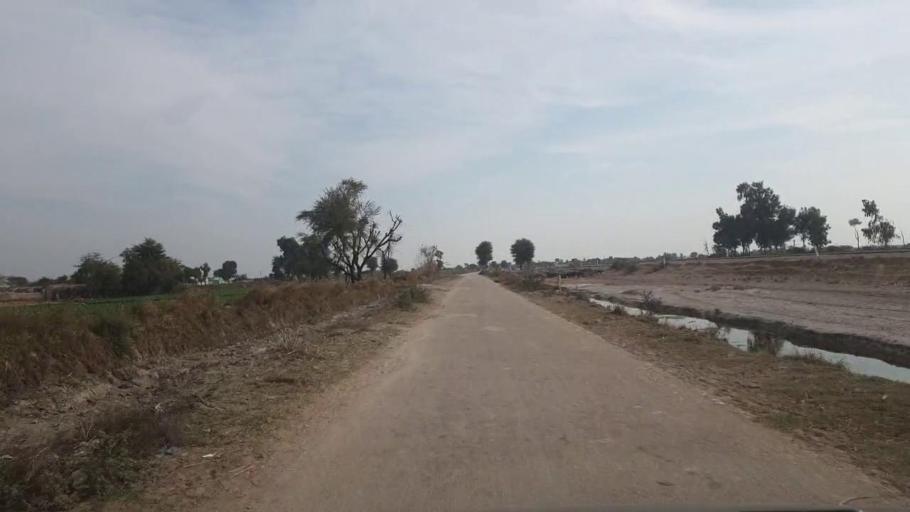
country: PK
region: Sindh
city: Nawabshah
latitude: 26.0883
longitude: 68.4860
